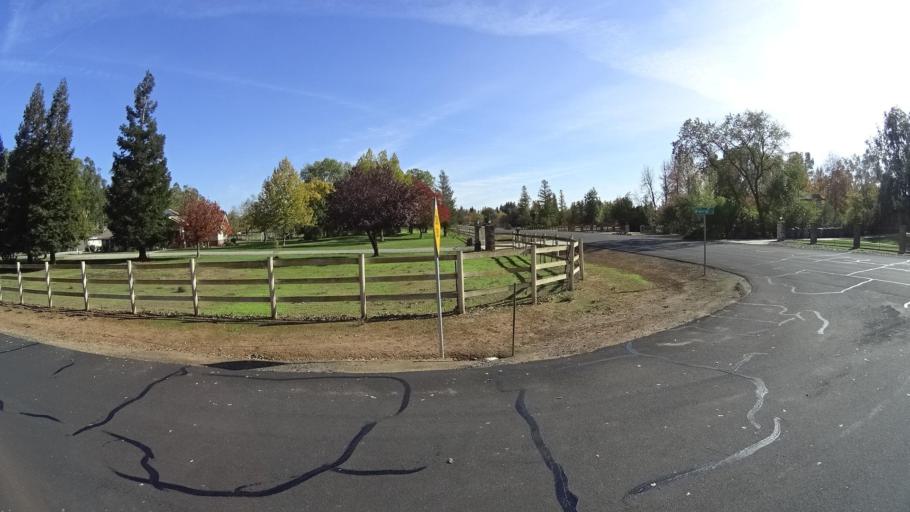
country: US
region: California
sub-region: Sacramento County
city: Wilton
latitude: 38.4359
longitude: -121.2896
